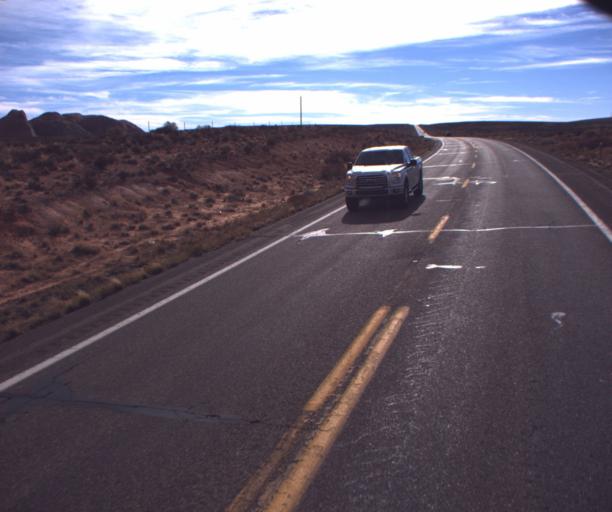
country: US
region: Arizona
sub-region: Coconino County
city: LeChee
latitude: 36.8436
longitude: -111.3286
